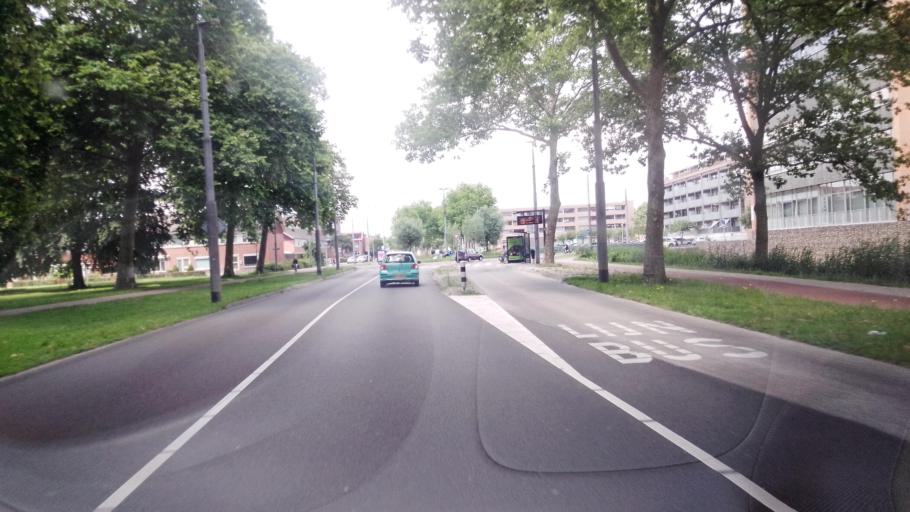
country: NL
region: Gelderland
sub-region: Gemeente Arnhem
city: Arnhem
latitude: 51.9610
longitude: 5.9225
